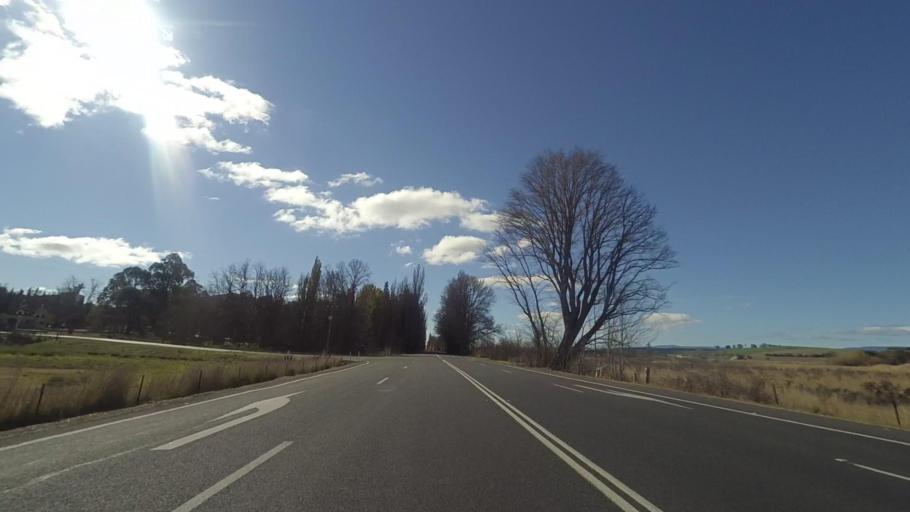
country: AU
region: New South Wales
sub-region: Bathurst Regional
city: Perthville
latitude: -33.4655
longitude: 149.5702
